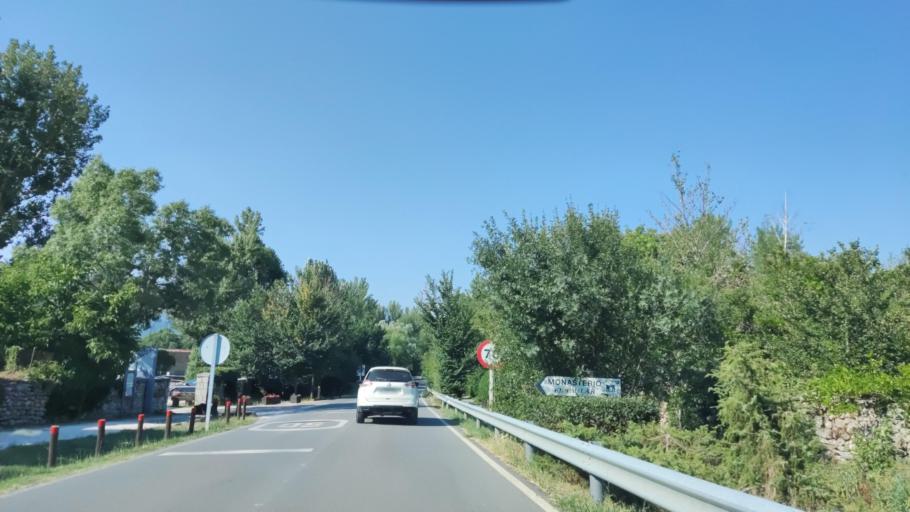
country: ES
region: Madrid
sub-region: Provincia de Madrid
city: Rascafria
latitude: 40.8877
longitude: -3.8866
